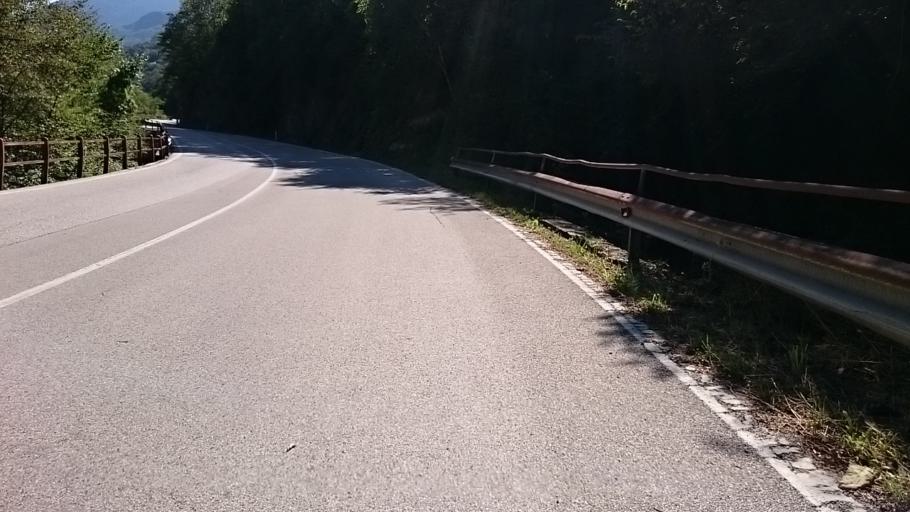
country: IT
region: Veneto
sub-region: Provincia di Belluno
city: Castello Lavazzo
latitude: 46.3000
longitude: 12.3156
